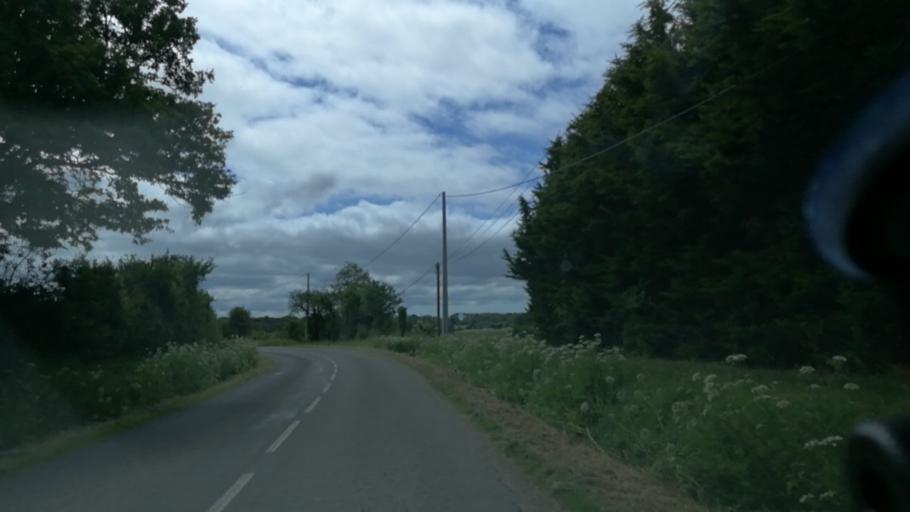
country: FR
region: Brittany
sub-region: Departement du Morbihan
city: Penestin
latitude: 47.4662
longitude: -2.4310
